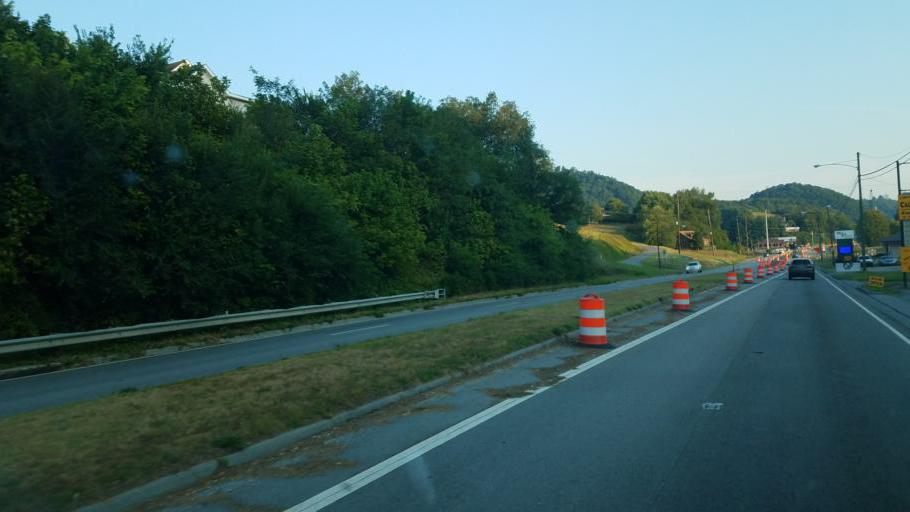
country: US
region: Virginia
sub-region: Scott County
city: Weber City
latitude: 36.6129
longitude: -82.5683
